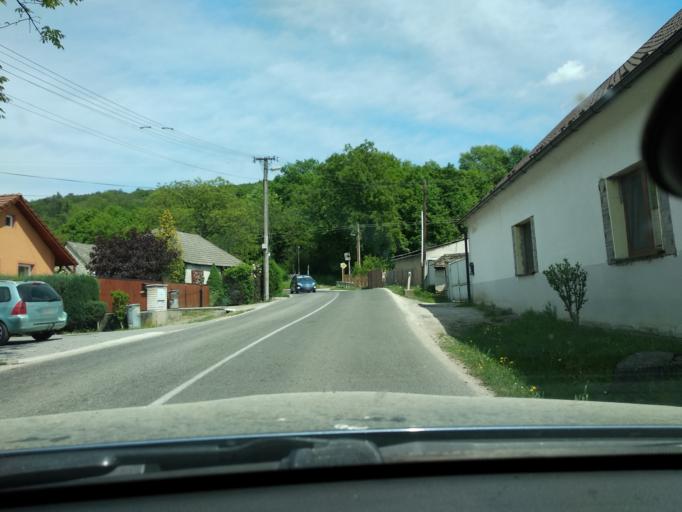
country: SK
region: Trenciansky
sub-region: Okres Nove Mesto nad Vahom
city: Nove Mesto nad Vahom
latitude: 48.8037
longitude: 17.8583
